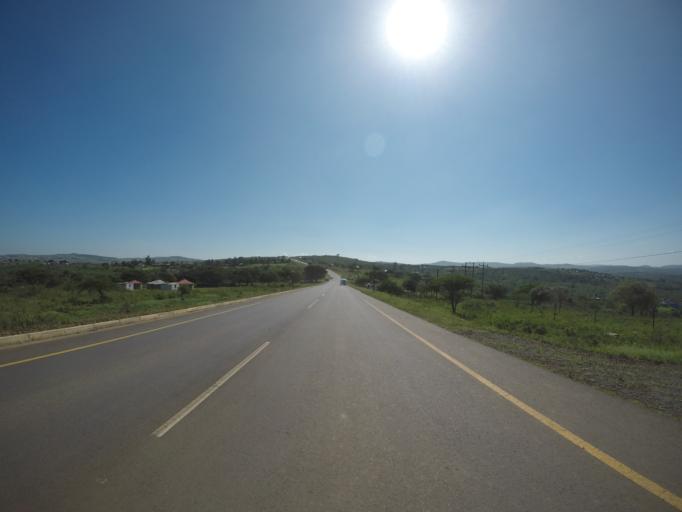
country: ZA
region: KwaZulu-Natal
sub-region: uThungulu District Municipality
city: Empangeni
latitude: -28.5623
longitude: 31.7054
